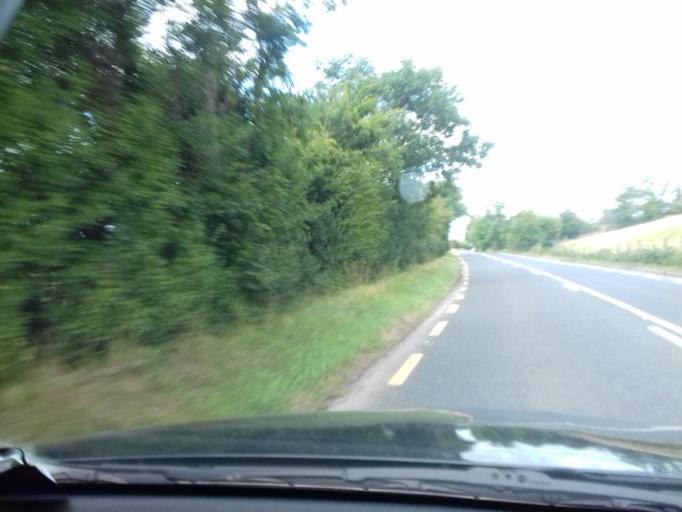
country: IE
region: Leinster
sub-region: Wicklow
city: Valleymount
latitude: 53.0546
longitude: -6.6274
